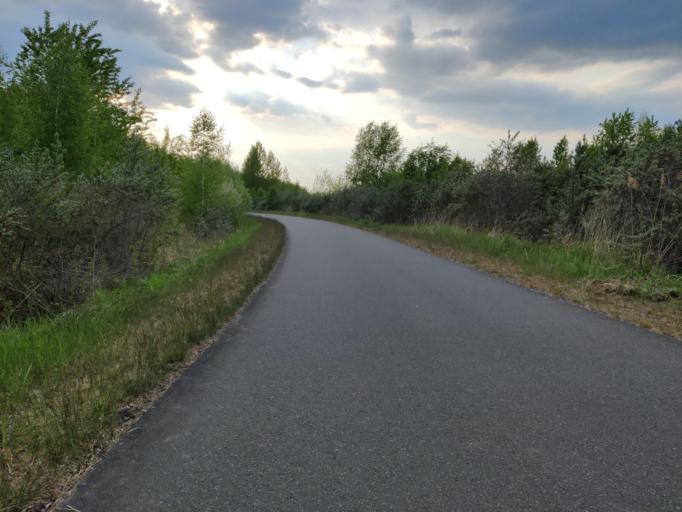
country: DE
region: Saxony
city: Rotha
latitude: 51.2450
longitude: 12.4379
